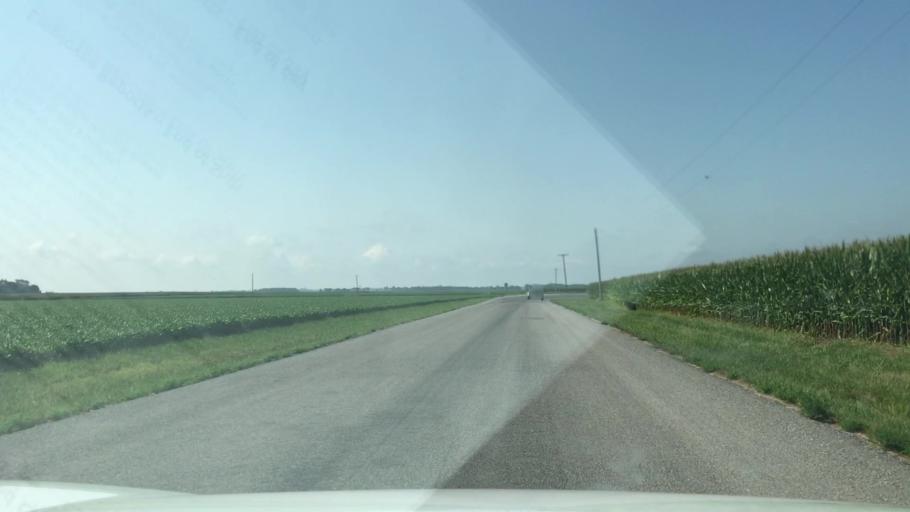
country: US
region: Illinois
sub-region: Washington County
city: Okawville
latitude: 38.4153
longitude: -89.4777
